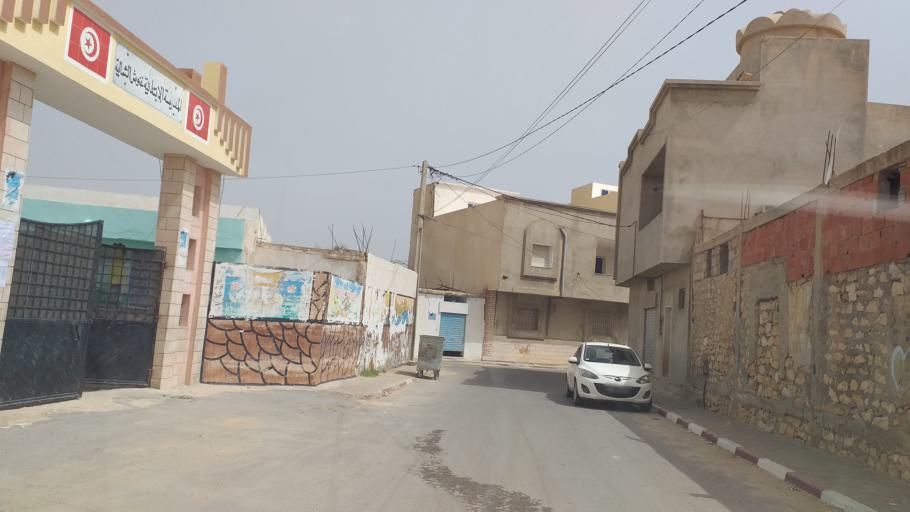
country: TN
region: Qabis
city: Gabes
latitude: 33.9419
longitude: 10.0630
